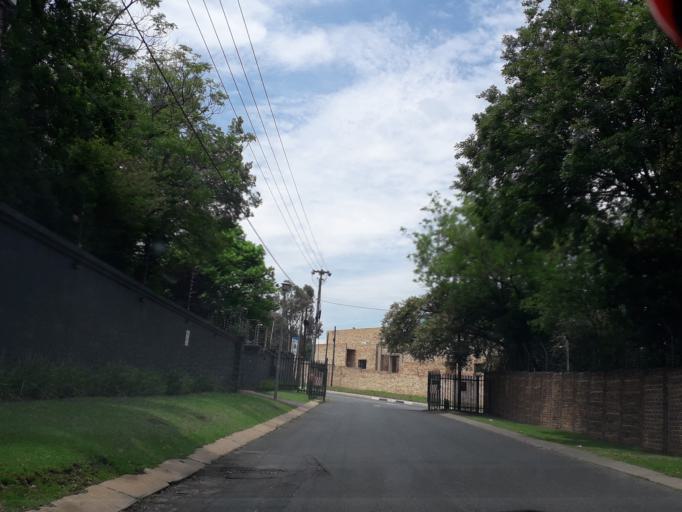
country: ZA
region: Gauteng
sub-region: City of Johannesburg Metropolitan Municipality
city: Midrand
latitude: -26.0593
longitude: 28.0562
